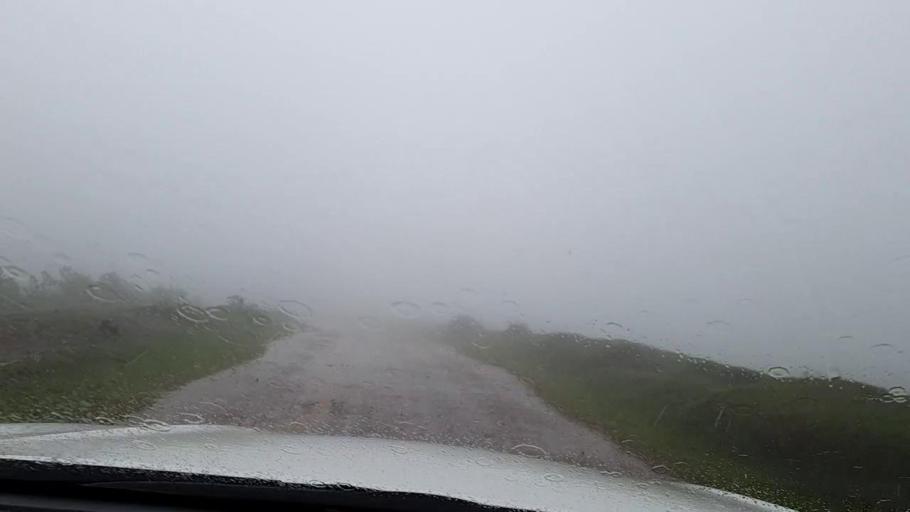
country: RW
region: Northern Province
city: Byumba
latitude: -1.7323
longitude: 30.0229
